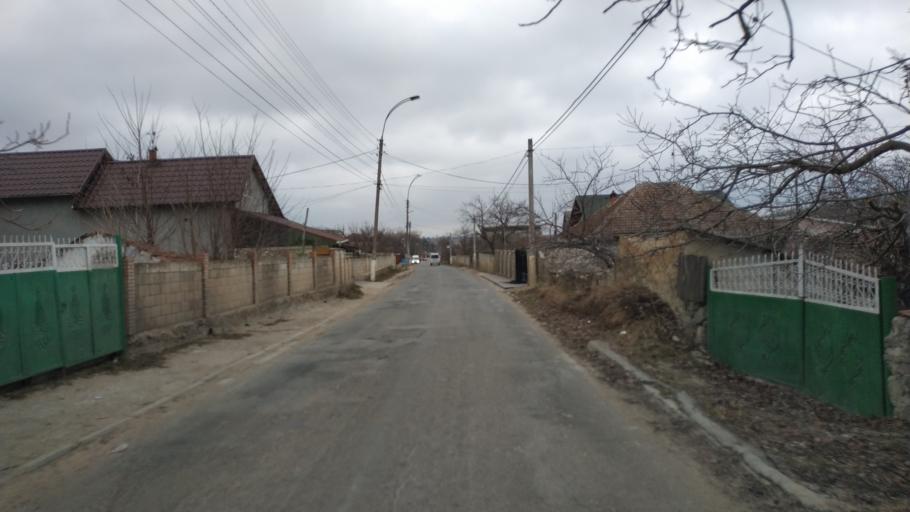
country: MD
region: Laloveni
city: Ialoveni
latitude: 46.9049
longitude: 28.8078
